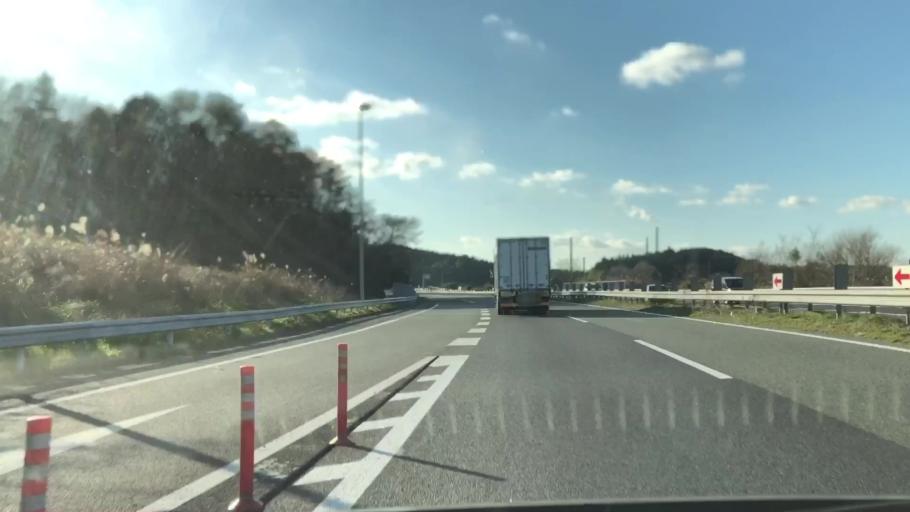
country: JP
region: Yamaguchi
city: Ogori-shimogo
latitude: 34.1705
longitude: 131.2464
